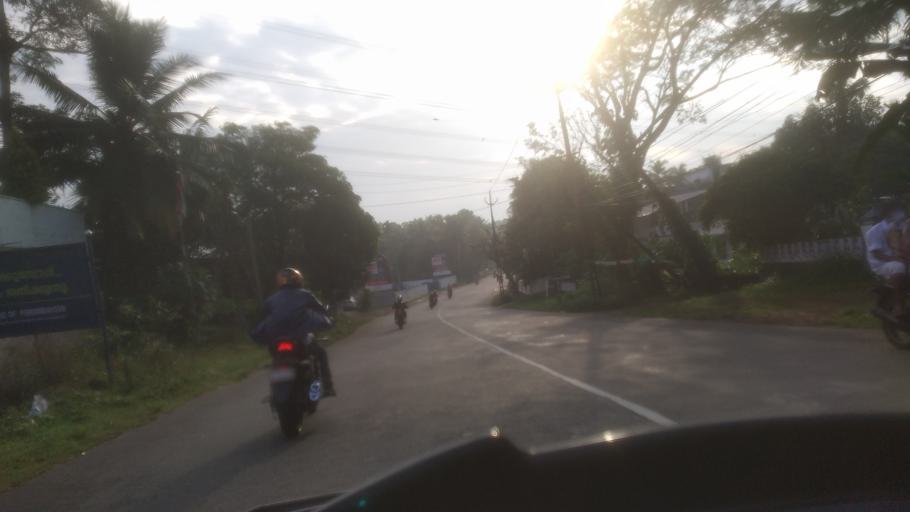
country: IN
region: Kerala
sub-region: Ernakulam
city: Perumpavur
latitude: 10.1156
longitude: 76.5012
